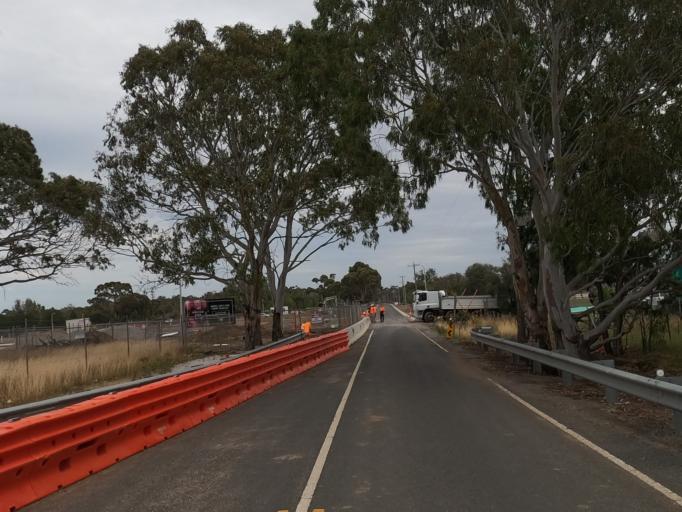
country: AU
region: Victoria
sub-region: Hume
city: Greenvale
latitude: -37.6410
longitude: 144.8716
